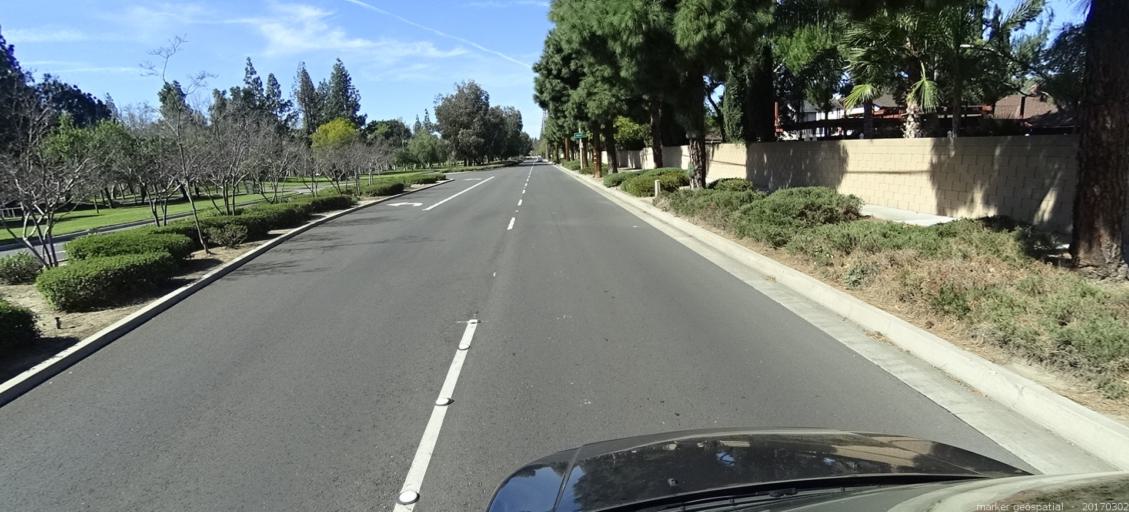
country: US
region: California
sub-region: Orange County
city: Yorba Linda
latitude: 33.8720
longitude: -117.7628
